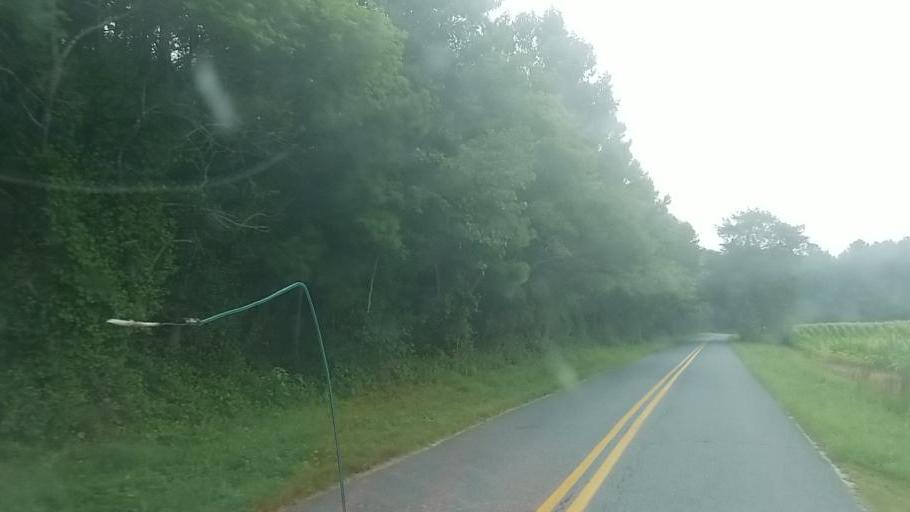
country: US
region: Maryland
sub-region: Wicomico County
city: Pittsville
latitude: 38.4311
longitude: -75.3218
